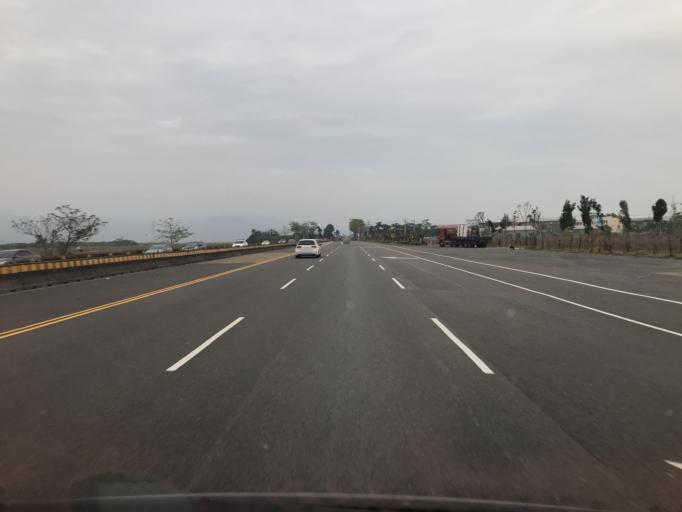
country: TW
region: Taiwan
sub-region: Pingtung
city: Pingtung
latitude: 22.4231
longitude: 120.5804
